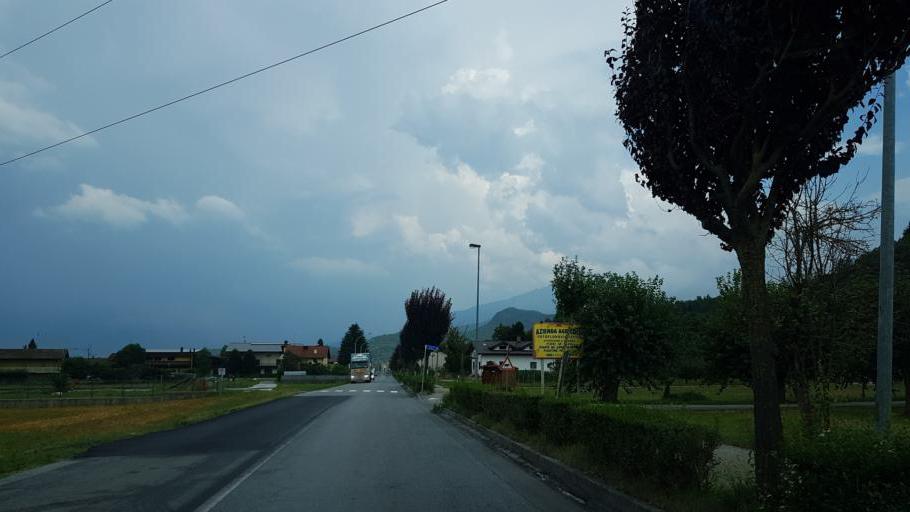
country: IT
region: Piedmont
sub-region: Provincia di Cuneo
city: Roccavione
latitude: 44.3340
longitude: 7.4675
